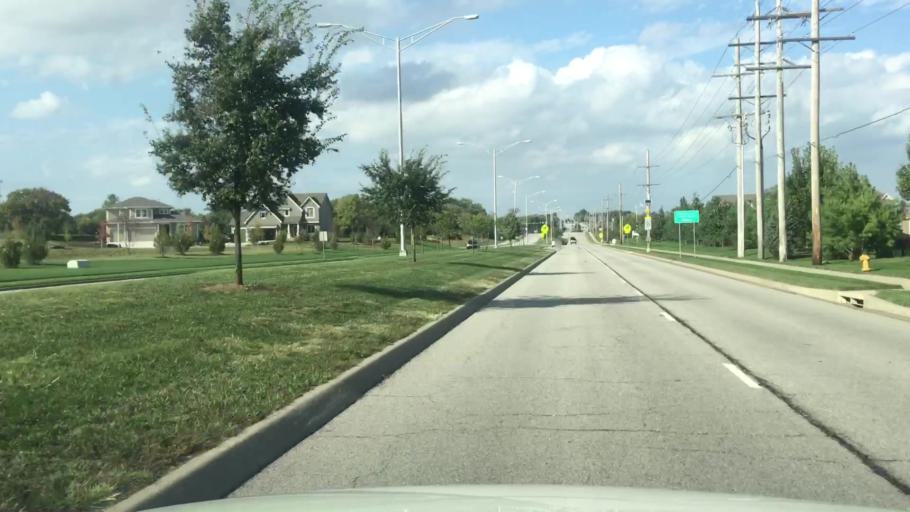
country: US
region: Kansas
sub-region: Johnson County
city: Lenexa
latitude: 38.8287
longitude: -94.6863
